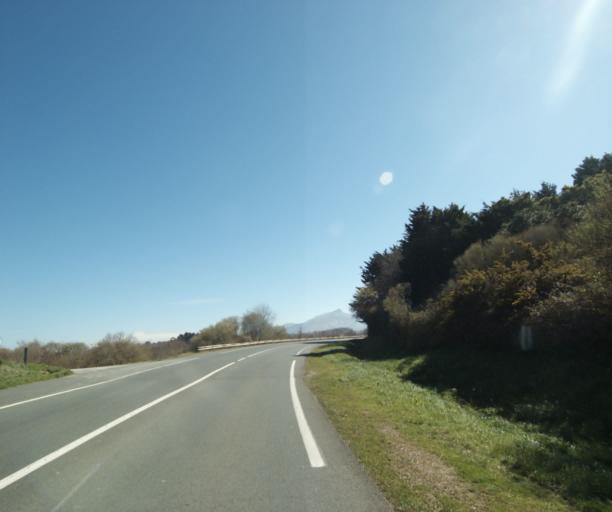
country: FR
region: Aquitaine
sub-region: Departement des Pyrenees-Atlantiques
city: Ciboure
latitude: 43.3901
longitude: -1.7004
